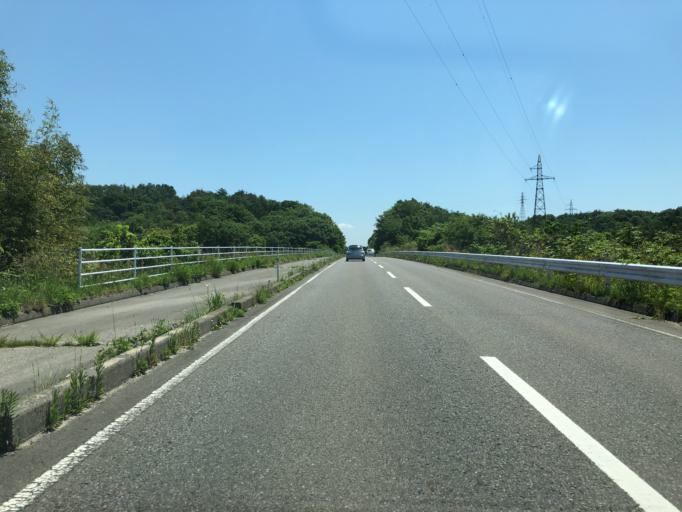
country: JP
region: Fukushima
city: Motomiya
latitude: 37.5320
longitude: 140.4248
